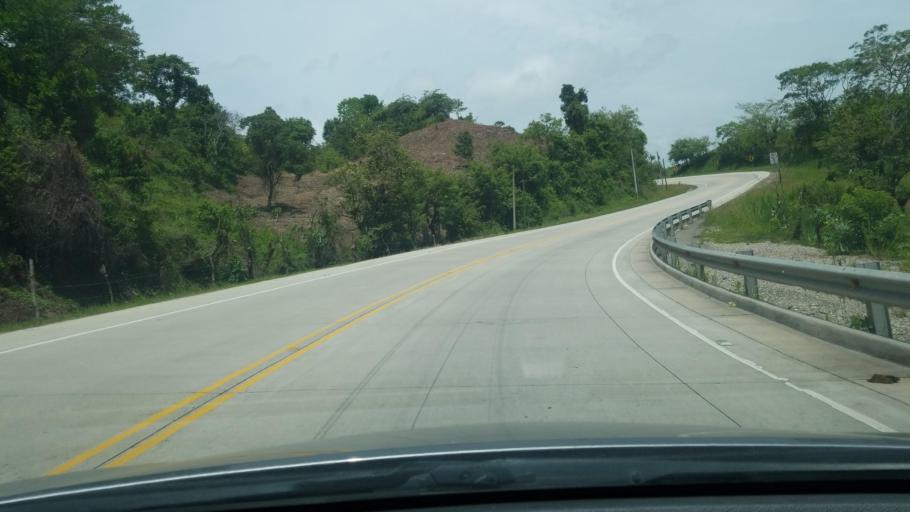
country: HN
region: Copan
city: Agua Caliente
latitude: 14.8554
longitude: -88.7970
